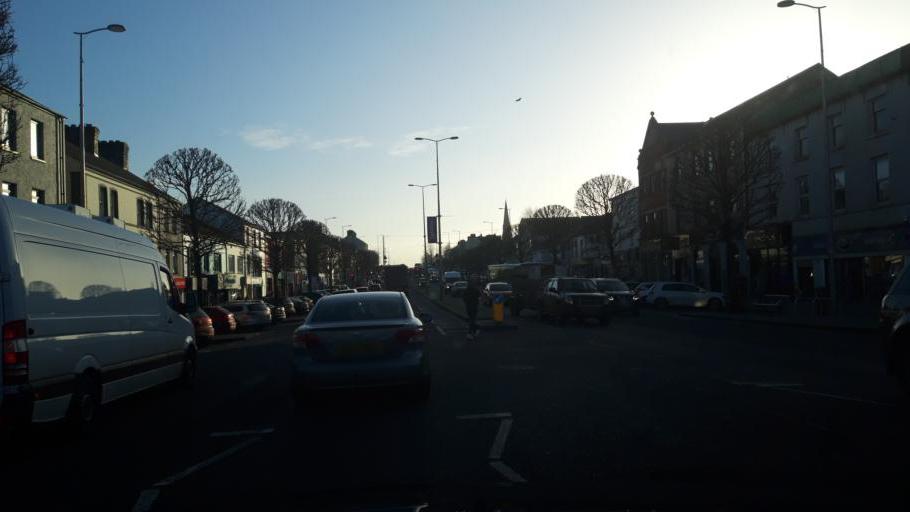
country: GB
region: Northern Ireland
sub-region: Cookstown District
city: Cookstown
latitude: 54.6470
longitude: -6.7451
